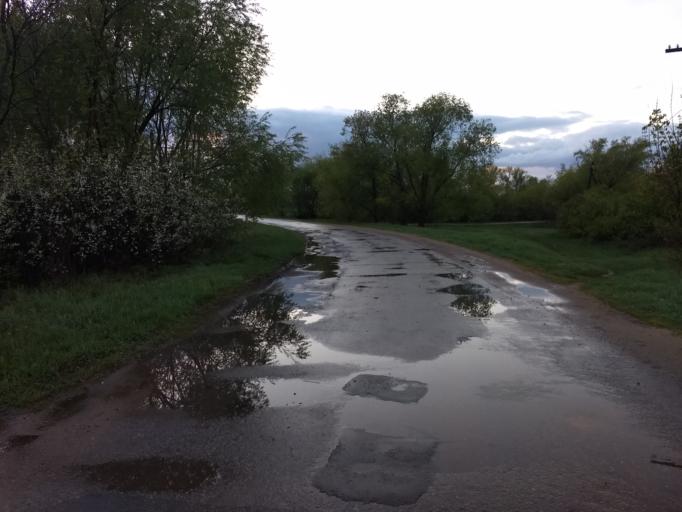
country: RU
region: Lipetsk
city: Zadonsk
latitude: 52.2921
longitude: 38.9499
